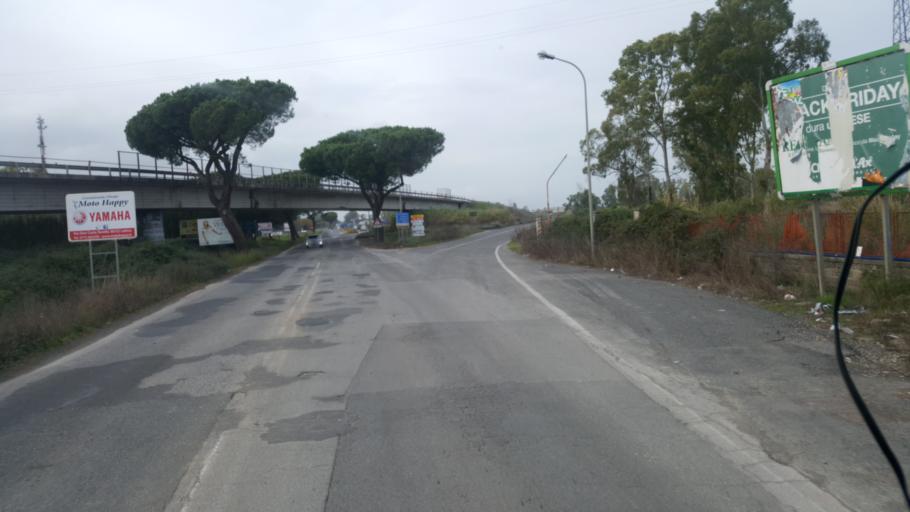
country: IT
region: Latium
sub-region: Provincia di Latina
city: Borgo Podgora
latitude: 41.4829
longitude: 12.8610
